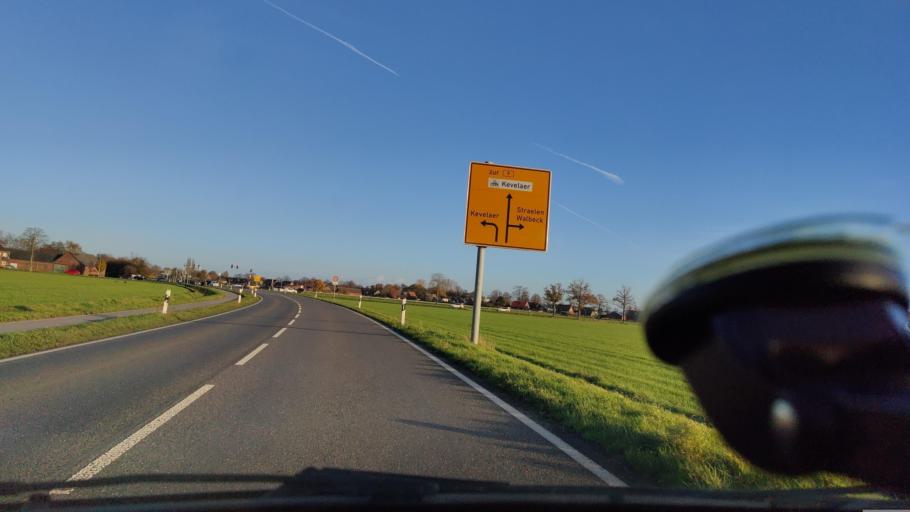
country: DE
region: North Rhine-Westphalia
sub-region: Regierungsbezirk Dusseldorf
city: Kevelaer
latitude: 51.5670
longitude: 6.2401
